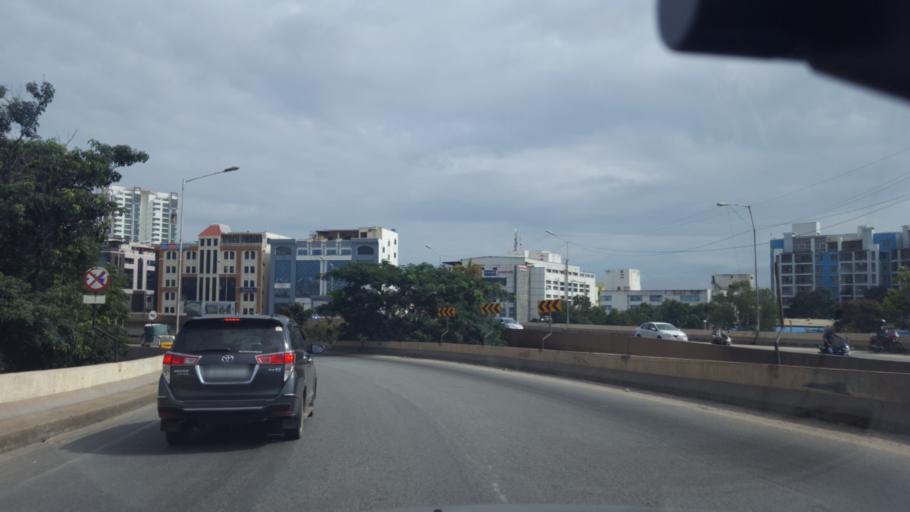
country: IN
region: Karnataka
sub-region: Bangalore Urban
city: Bangalore
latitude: 12.9960
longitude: 77.6649
